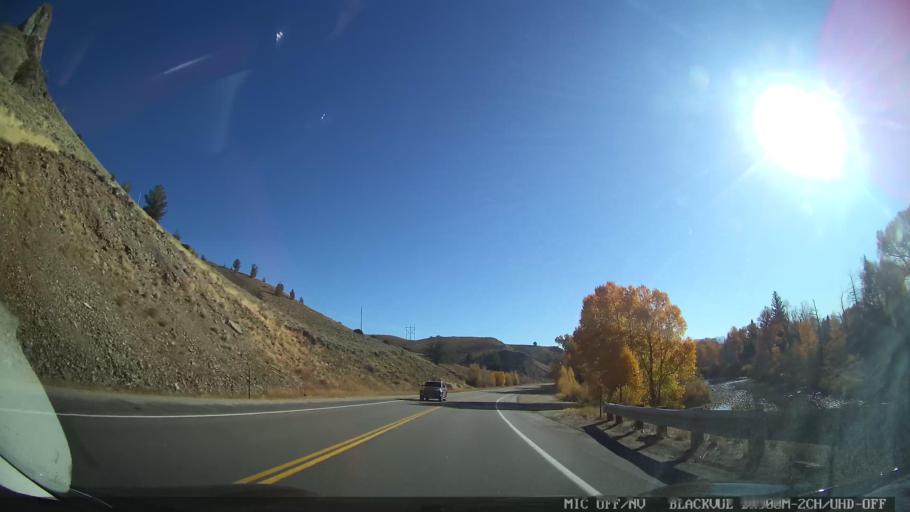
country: US
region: Colorado
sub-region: Grand County
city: Granby
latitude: 40.1100
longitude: -105.9992
